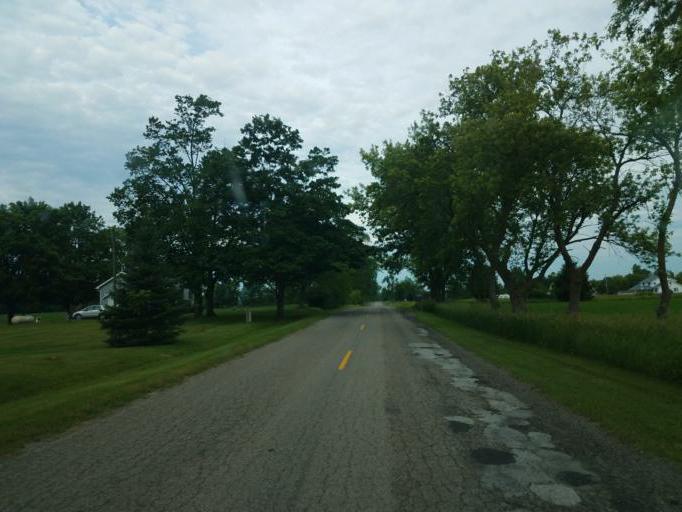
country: US
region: Michigan
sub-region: Barry County
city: Nashville
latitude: 42.6905
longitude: -84.9865
